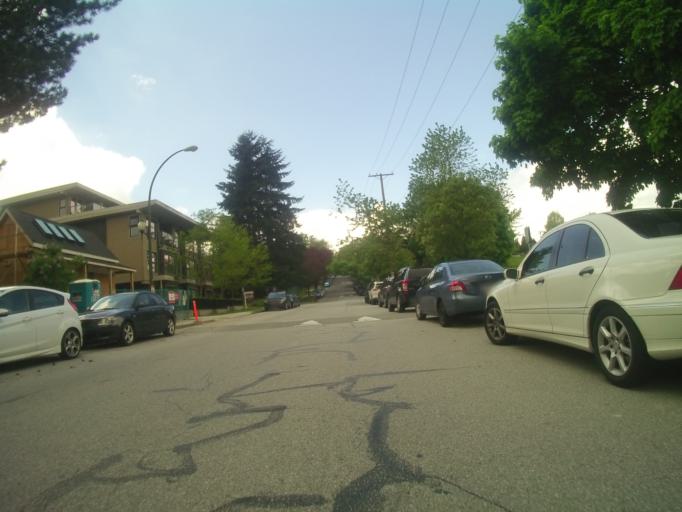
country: CA
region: British Columbia
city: Vancouver
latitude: 49.2643
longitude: -123.0823
